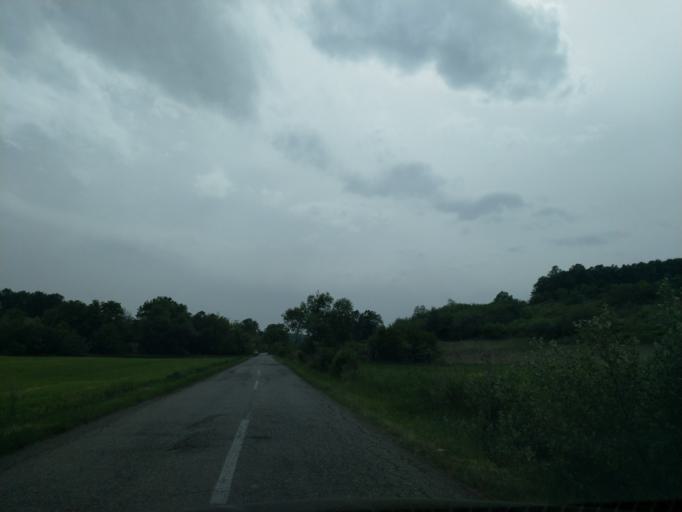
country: RS
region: Central Serbia
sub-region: Pomoravski Okrug
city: Paracin
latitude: 43.8711
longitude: 21.5441
